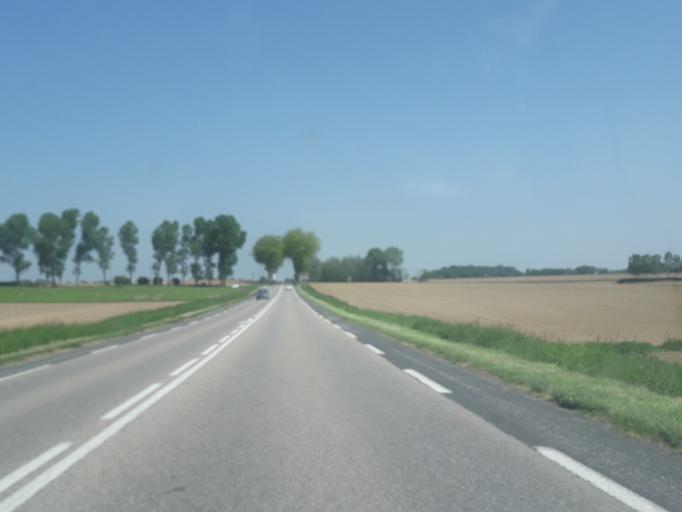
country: FR
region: Rhone-Alpes
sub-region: Departement de l'Ain
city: Mionnay
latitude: 45.9099
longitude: 4.9389
